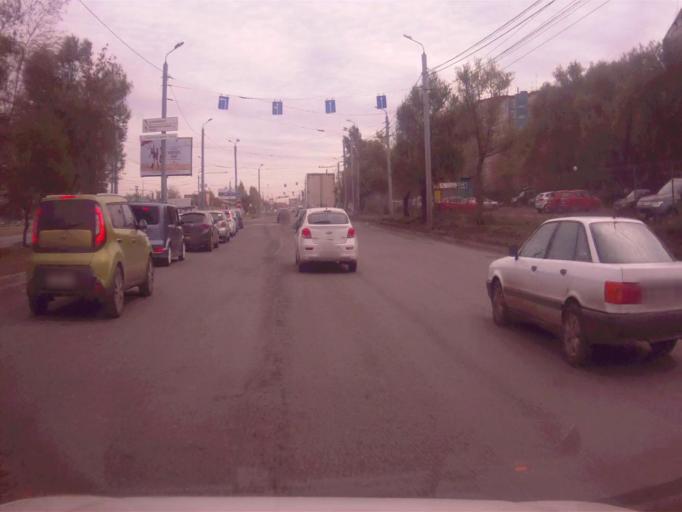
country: RU
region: Chelyabinsk
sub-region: Gorod Chelyabinsk
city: Chelyabinsk
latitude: 55.1441
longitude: 61.4495
